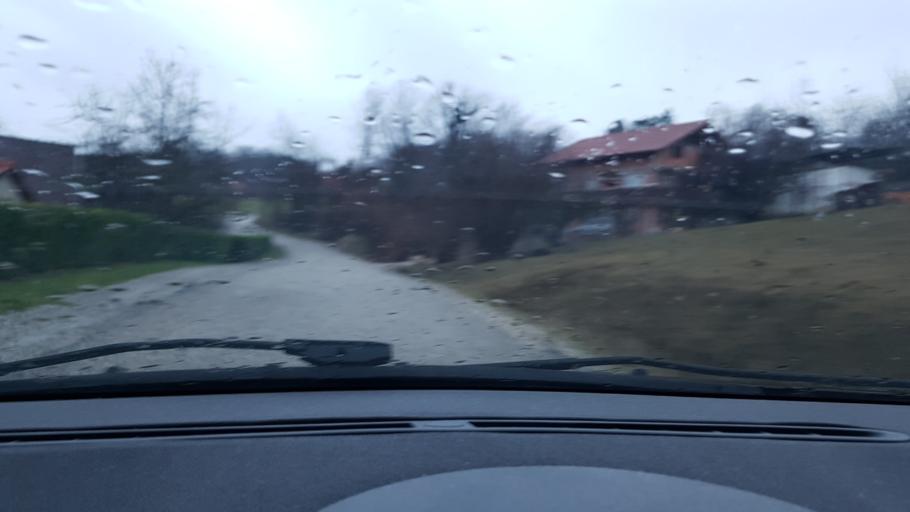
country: HR
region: Krapinsko-Zagorska
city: Bedekovcina
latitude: 45.9936
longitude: 15.9830
